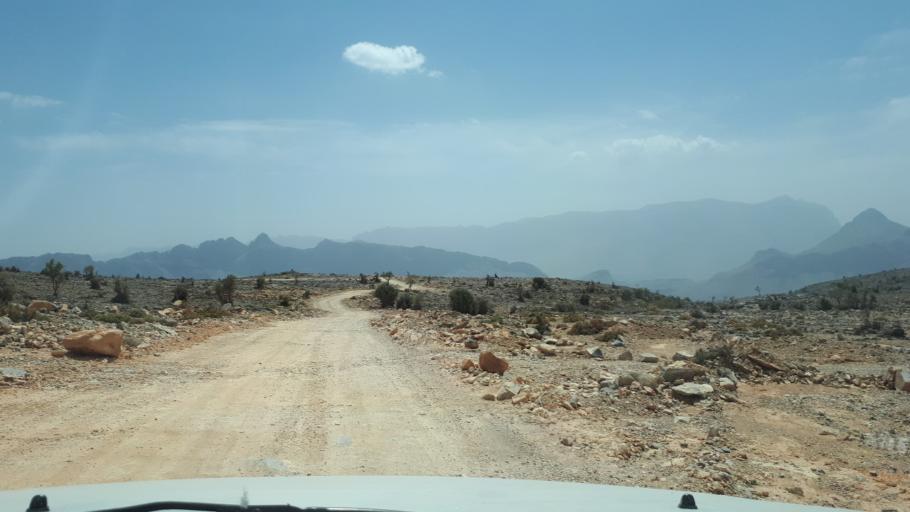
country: OM
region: Muhafazat ad Dakhiliyah
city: Bahla'
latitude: 23.1980
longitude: 57.2000
